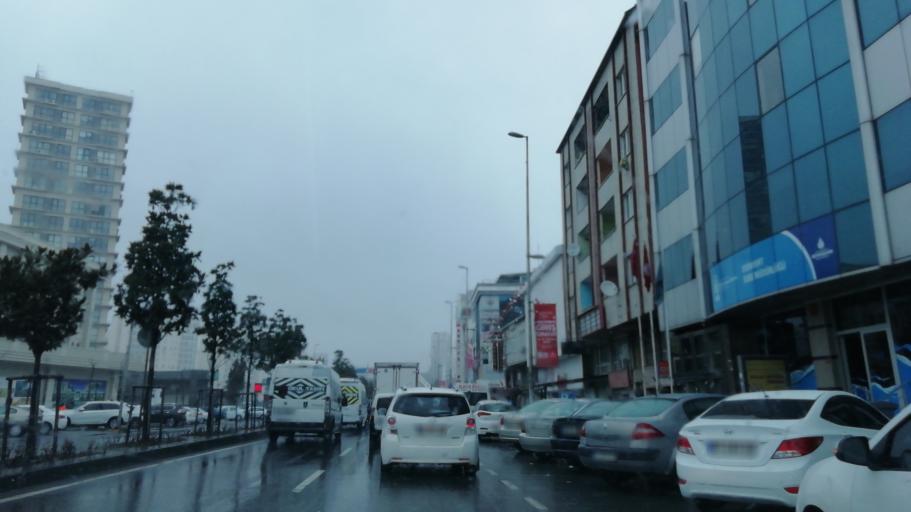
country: TR
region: Istanbul
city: Esenyurt
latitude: 41.0245
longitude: 28.6855
